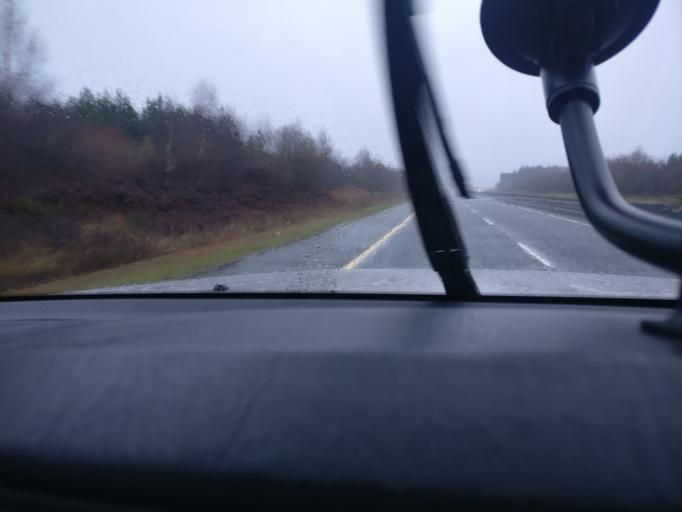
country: IE
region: Leinster
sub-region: An Iarmhi
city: Rochfortbridge
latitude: 53.4131
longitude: -7.2678
